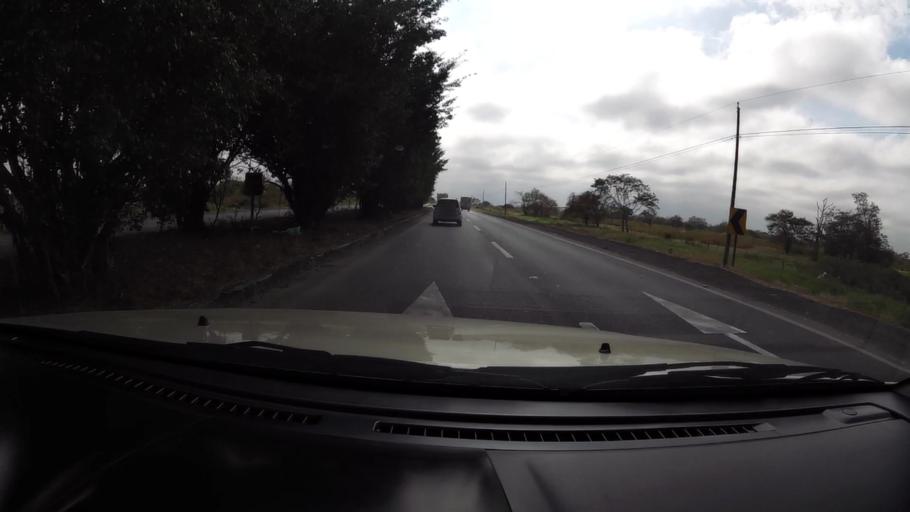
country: EC
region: Guayas
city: Eloy Alfaro
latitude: -2.1990
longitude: -79.7755
